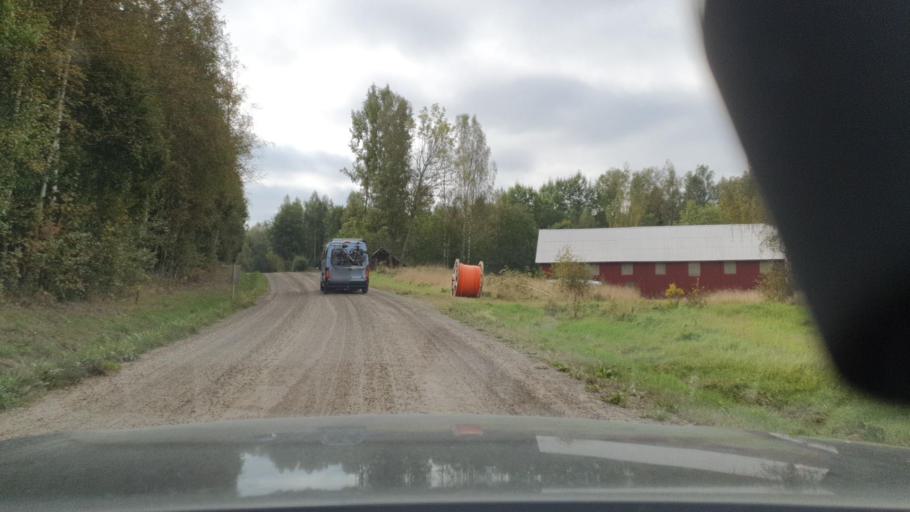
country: SE
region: Vaermland
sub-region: Eda Kommun
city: Amotfors
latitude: 59.7825
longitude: 12.3415
